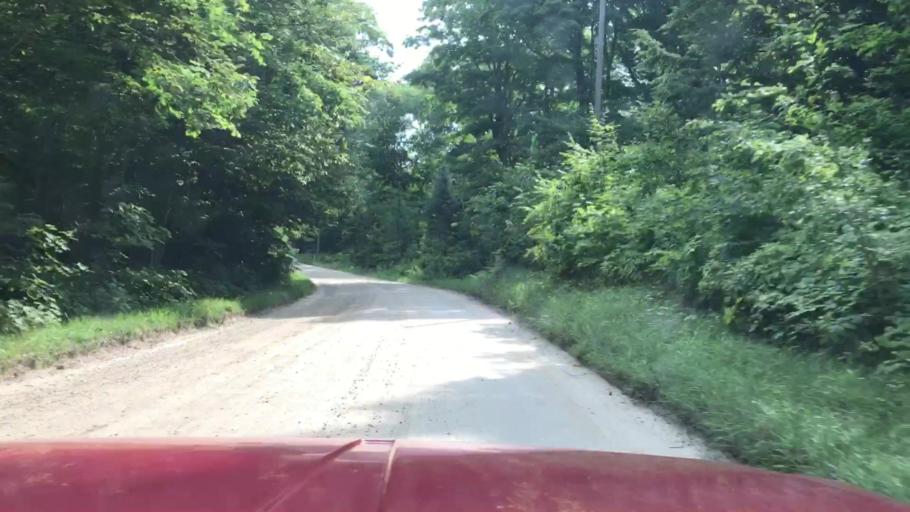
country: US
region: Michigan
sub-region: Charlevoix County
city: Charlevoix
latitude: 45.7454
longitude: -85.5538
